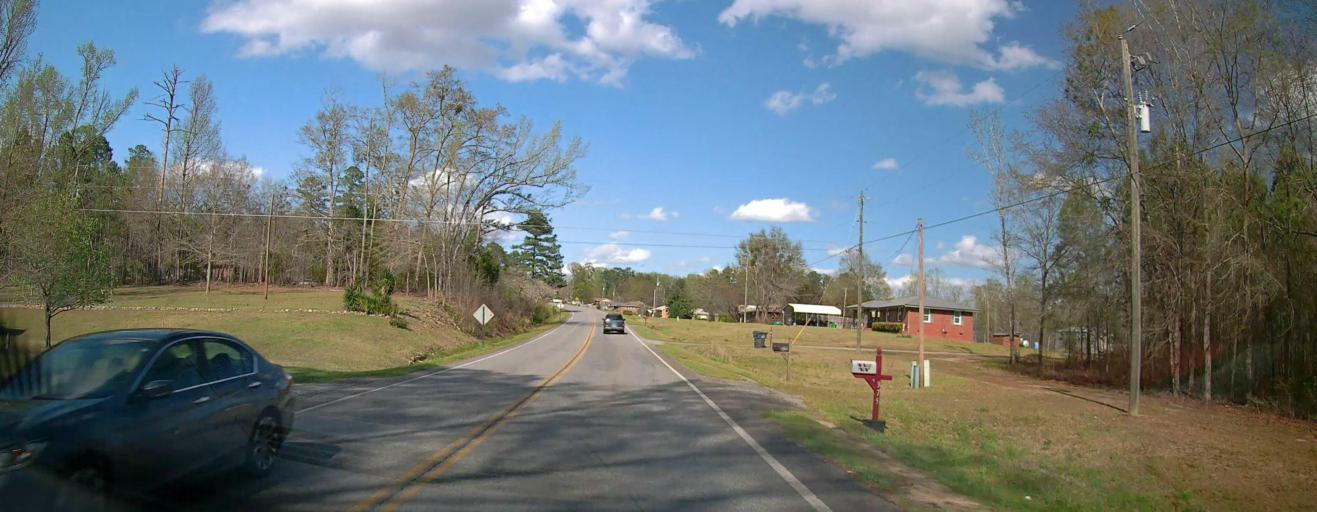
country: US
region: Georgia
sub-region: Baldwin County
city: Hardwick
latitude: 32.9947
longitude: -83.2614
